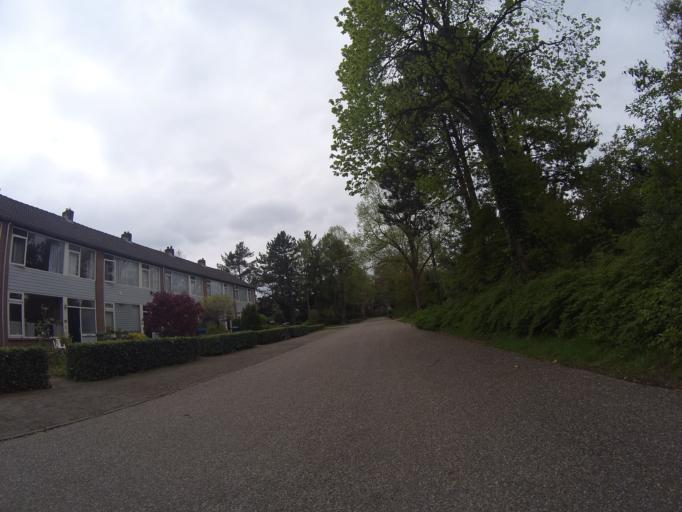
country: NL
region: Utrecht
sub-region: Gemeente Utrechtse Heuvelrug
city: Maarn
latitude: 52.0610
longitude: 5.3718
